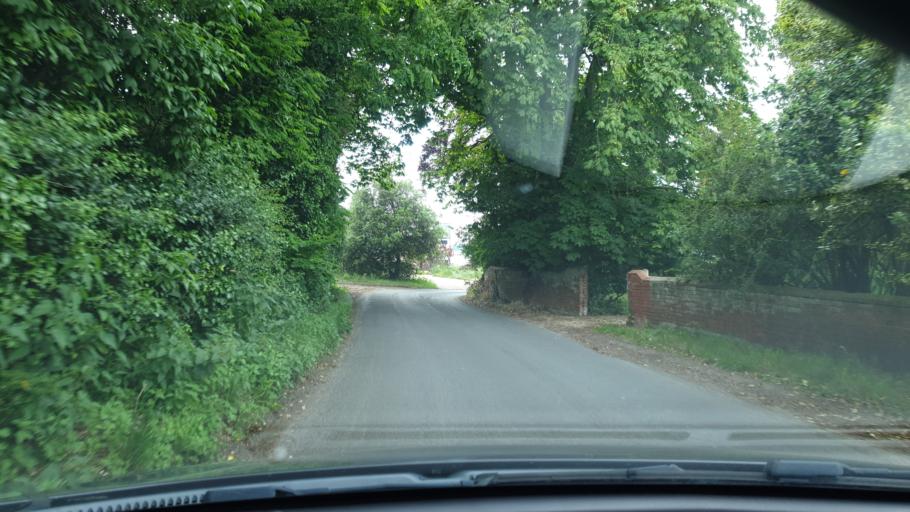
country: GB
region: England
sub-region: Suffolk
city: Shotley Gate
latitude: 51.9215
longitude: 1.2007
